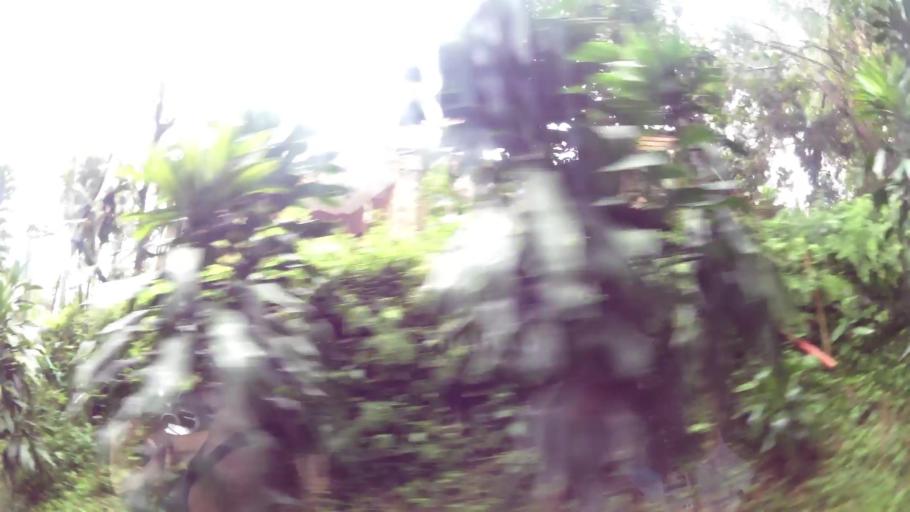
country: CO
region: Antioquia
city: Envigado
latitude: 6.1727
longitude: -75.5661
